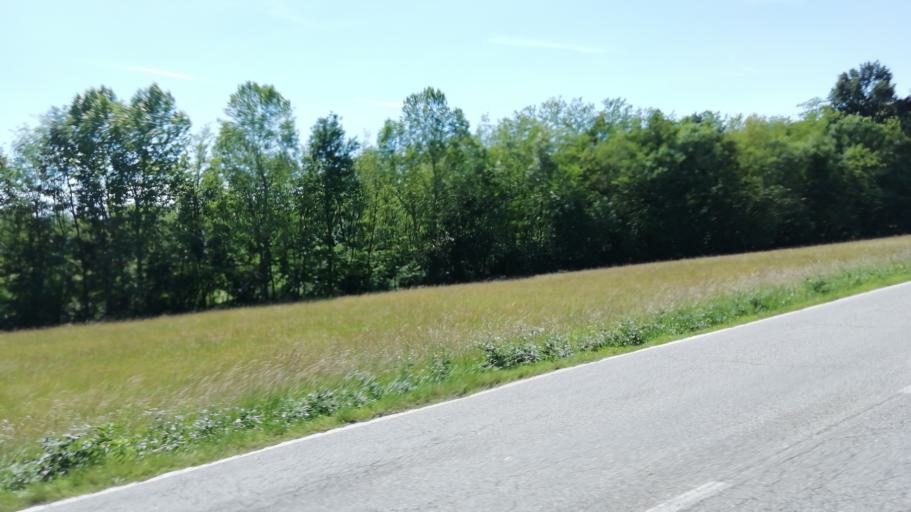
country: IT
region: Piedmont
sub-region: Provincia di Novara
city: Cressa
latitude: 45.6344
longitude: 8.5012
